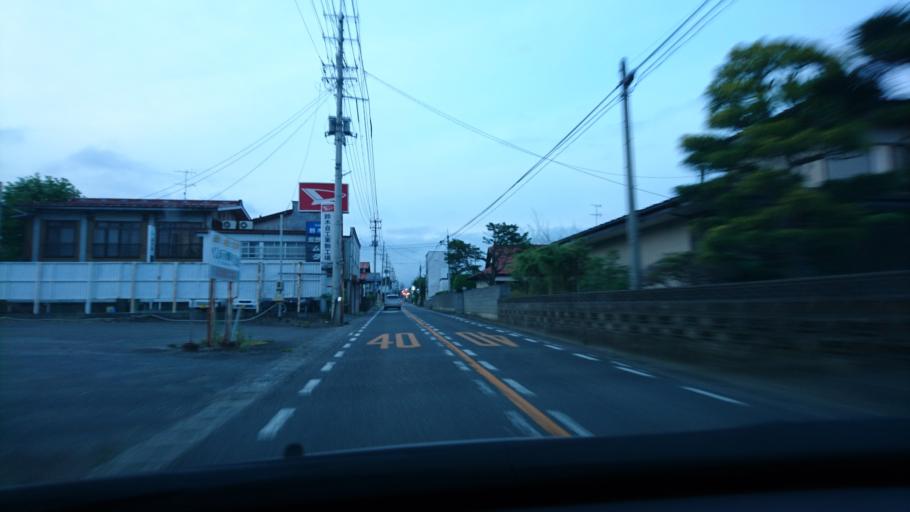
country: JP
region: Iwate
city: Ichinoseki
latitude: 38.8104
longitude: 140.9839
